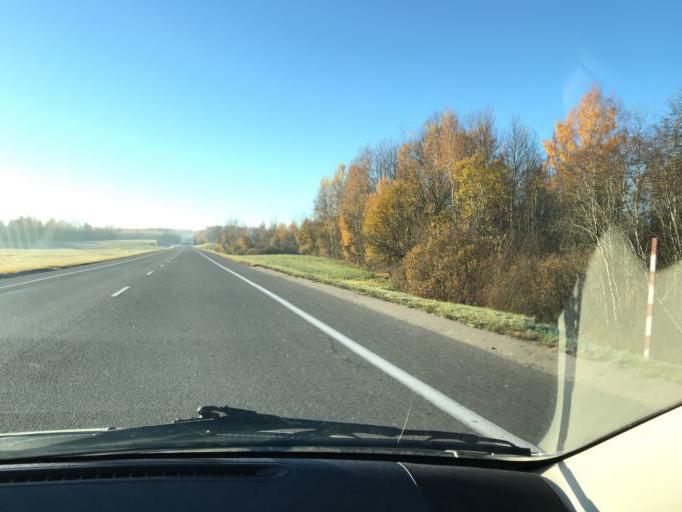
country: BY
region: Vitebsk
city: Vitebsk
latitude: 55.0730
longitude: 30.3082
